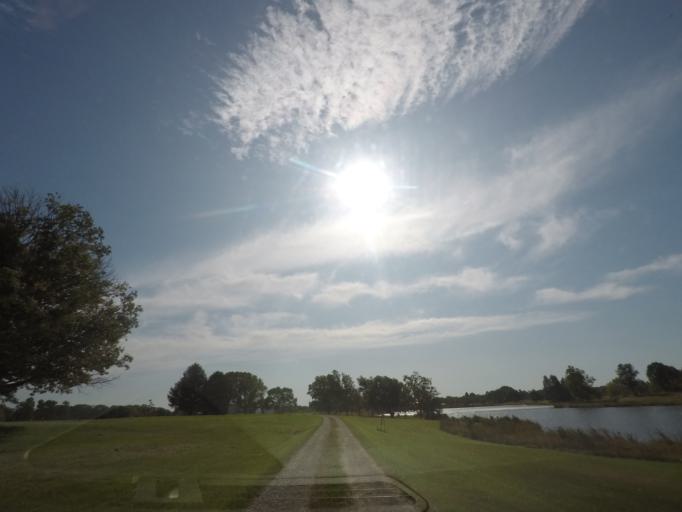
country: US
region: Iowa
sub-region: Story County
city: Gilbert
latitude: 42.1131
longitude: -93.5847
